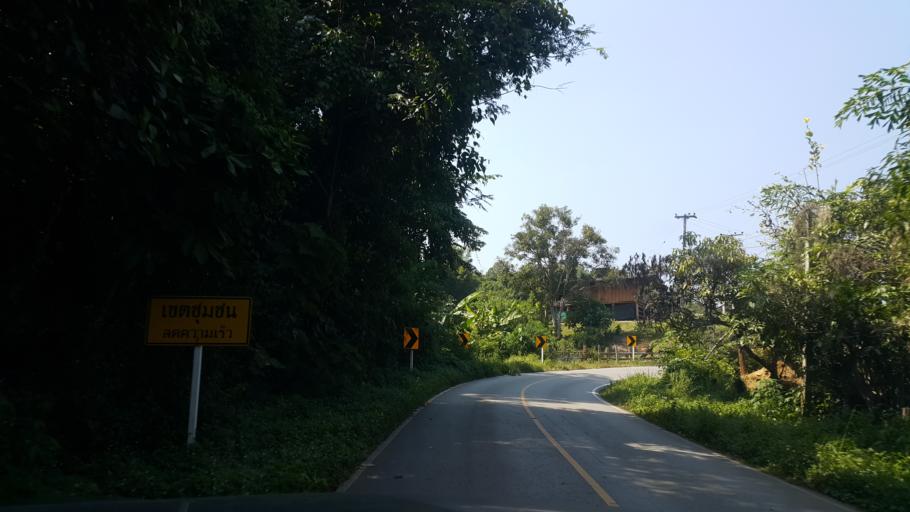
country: TH
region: Chiang Mai
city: Samoeng
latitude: 18.8647
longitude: 98.6371
